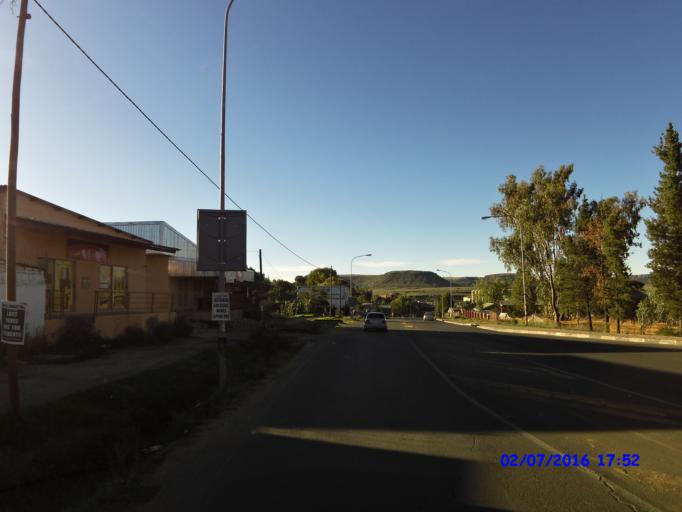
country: LS
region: Maseru
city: Maseru
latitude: -29.3070
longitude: 27.4848
